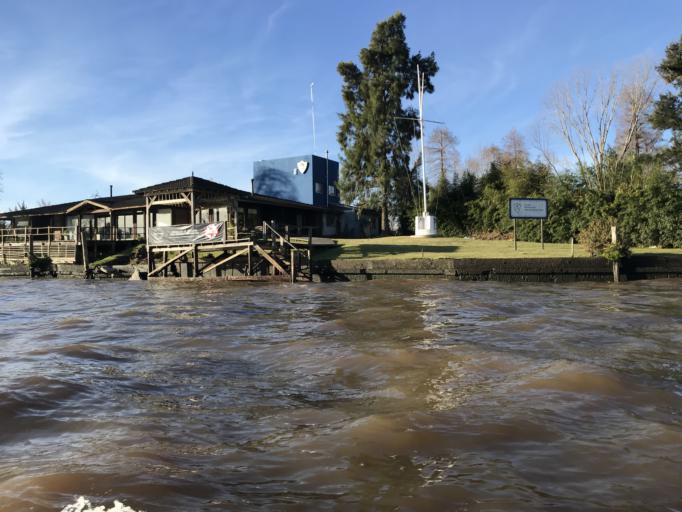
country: AR
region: Buenos Aires
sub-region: Partido de Tigre
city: Tigre
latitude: -34.4062
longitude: -58.5924
